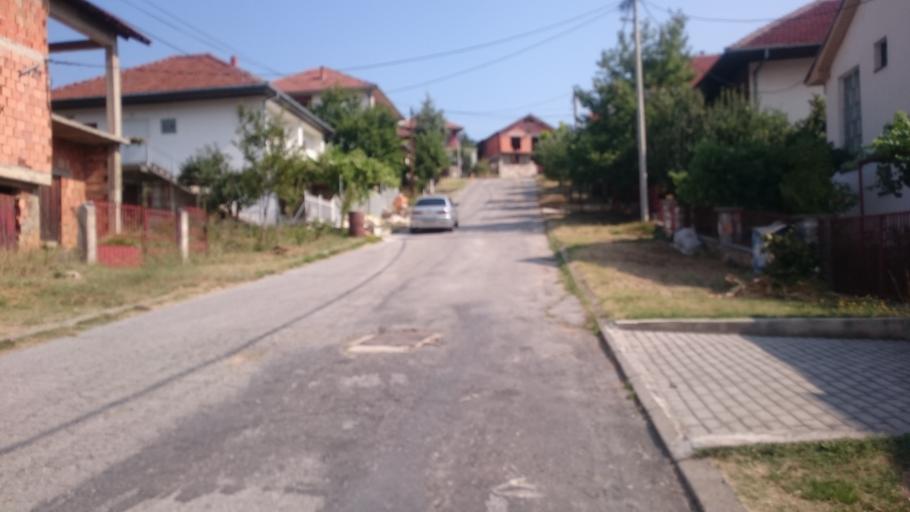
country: MK
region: Makedonski Brod
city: Makedonski Brod
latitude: 41.5154
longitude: 21.2153
